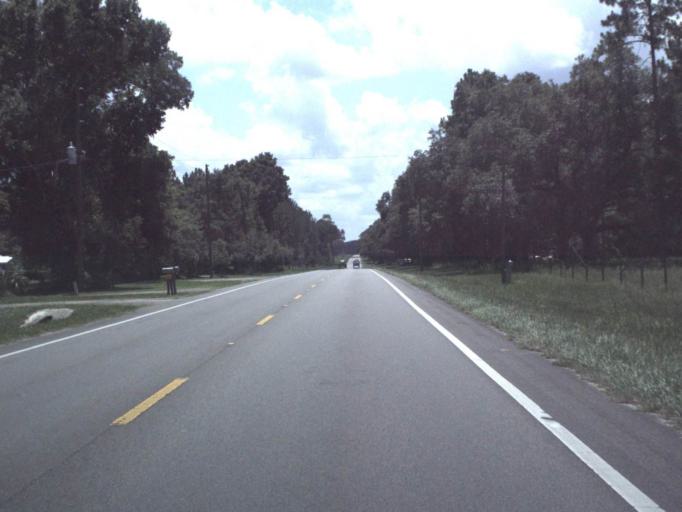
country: US
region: Florida
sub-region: Levy County
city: Williston
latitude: 29.4379
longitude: -82.4642
